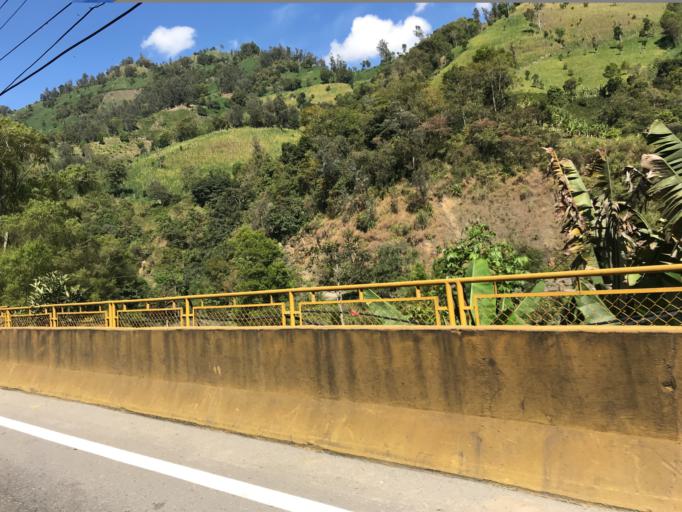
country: CO
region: Tolima
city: Cajamarca
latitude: 4.4358
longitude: -75.4451
